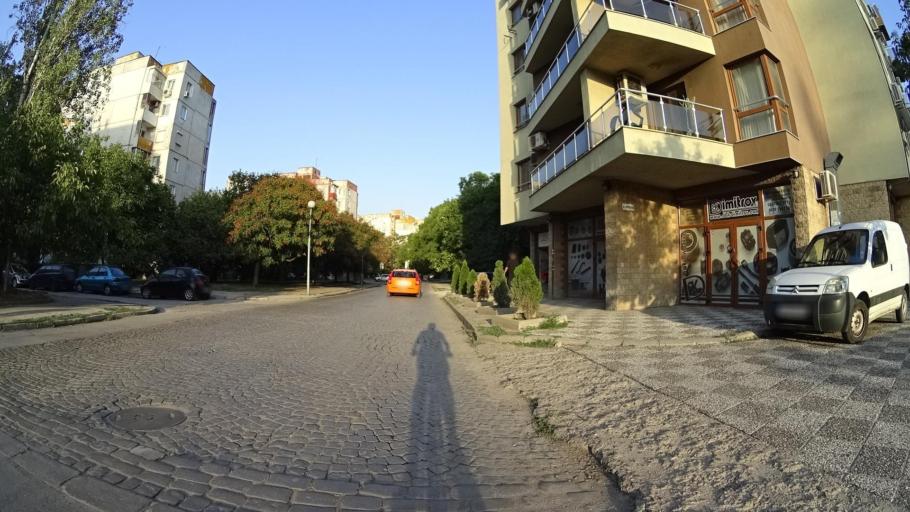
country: BG
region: Plovdiv
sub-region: Obshtina Plovdiv
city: Plovdiv
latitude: 42.1336
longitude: 24.7492
